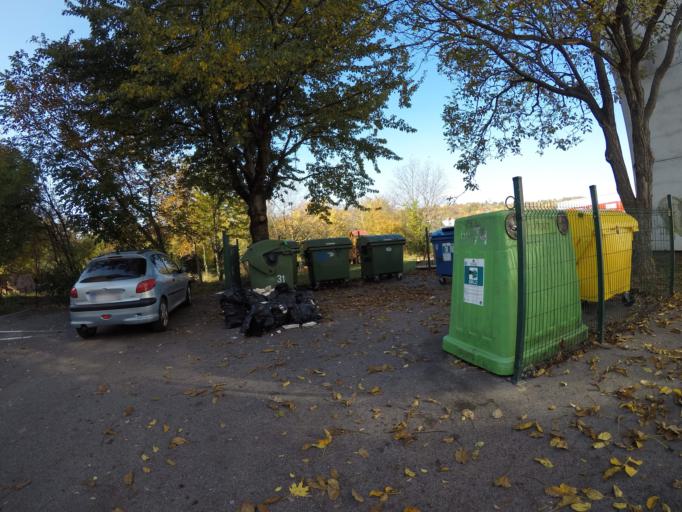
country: SK
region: Trenciansky
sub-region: Okres Nove Mesto nad Vahom
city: Nove Mesto nad Vahom
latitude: 48.7583
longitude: 17.8207
